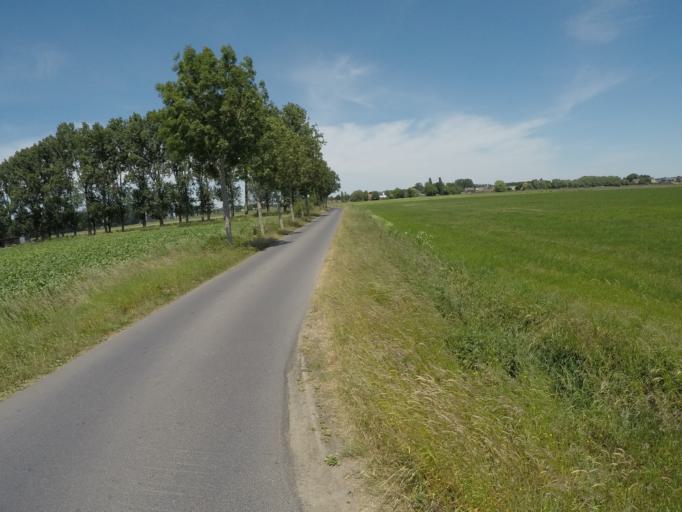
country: BE
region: Flanders
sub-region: Provincie Antwerpen
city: Wuustwezel
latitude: 51.3941
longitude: 4.6258
